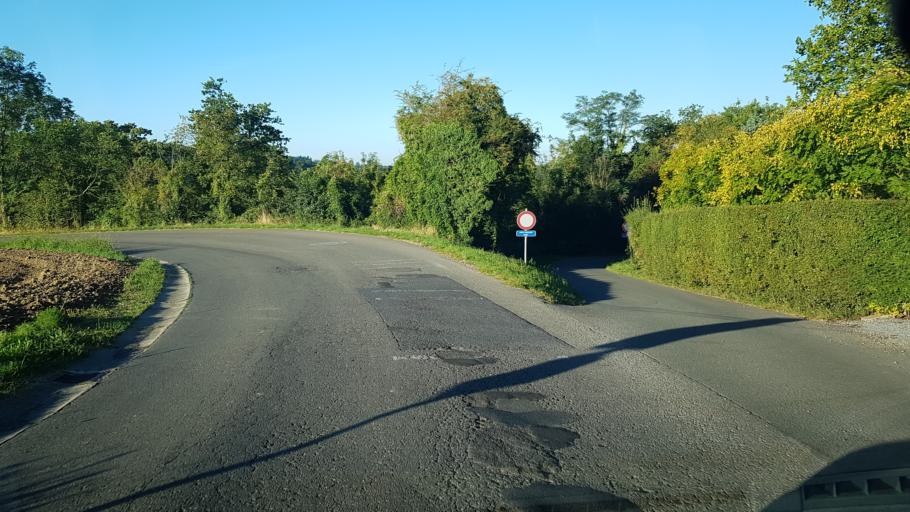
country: BE
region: Wallonia
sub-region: Province de Liege
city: Wanze
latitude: 50.5886
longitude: 5.1954
